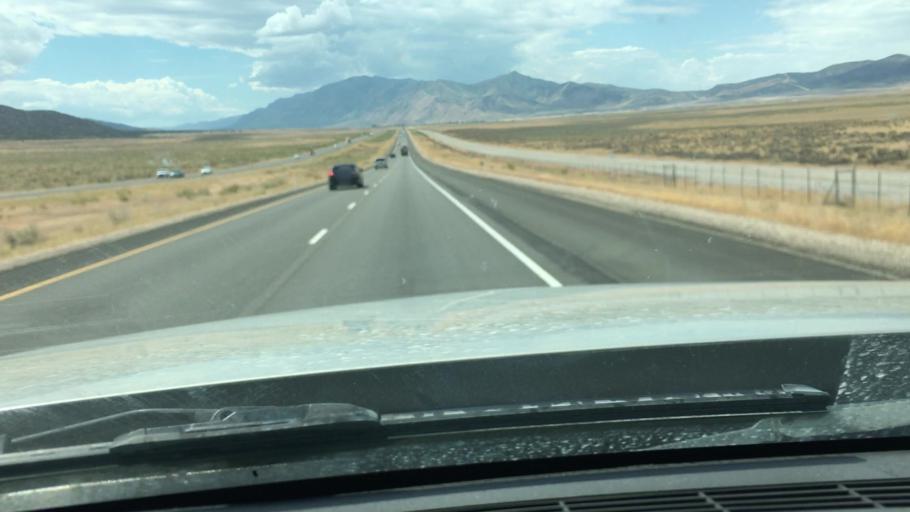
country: US
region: Utah
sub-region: Sanpete County
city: Gunnison
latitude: 39.3224
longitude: -112.0840
